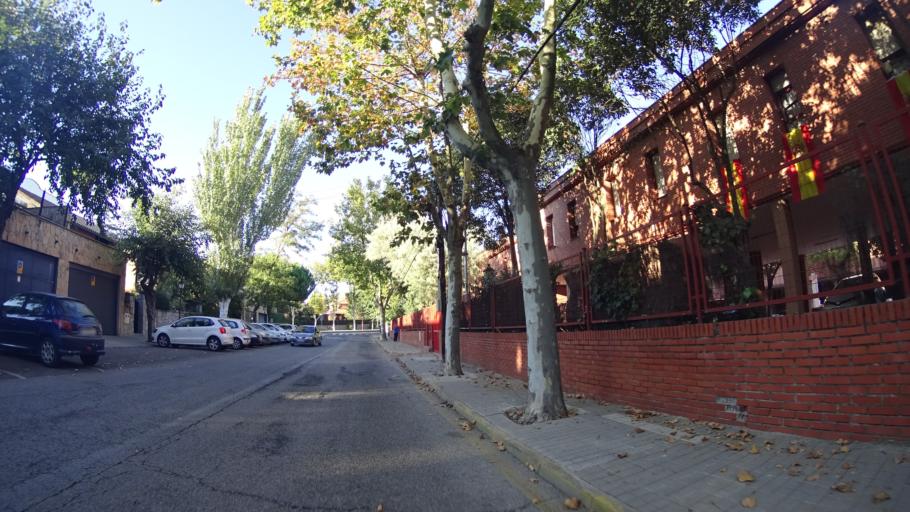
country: ES
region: Madrid
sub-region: Provincia de Madrid
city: Torrelodones
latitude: 40.5761
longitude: -3.9484
